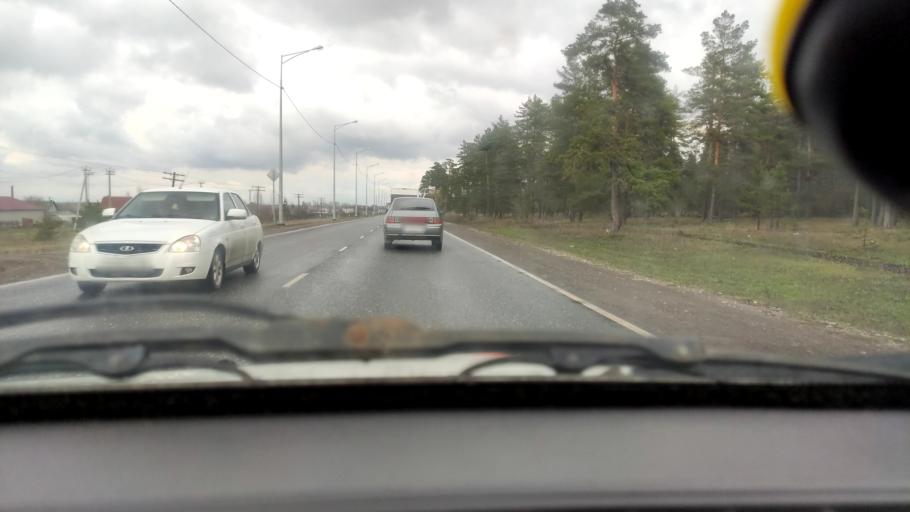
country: RU
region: Samara
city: Zhigulevsk
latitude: 53.5792
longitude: 49.5628
